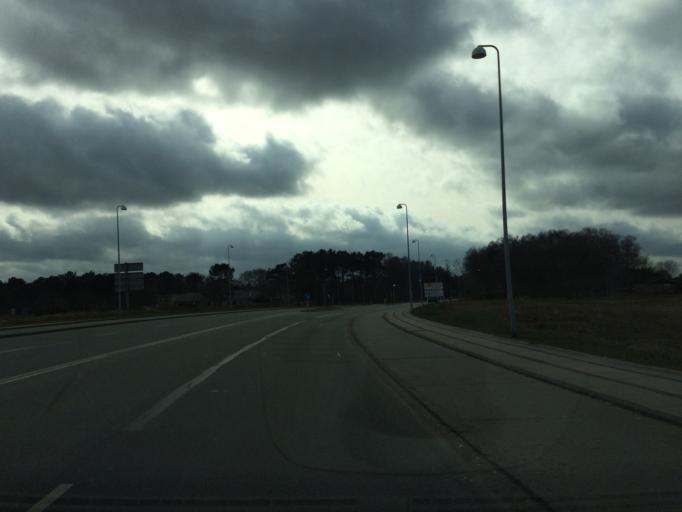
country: DK
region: Central Jutland
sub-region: Norddjurs Kommune
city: Grenaa
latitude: 56.4063
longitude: 10.9185
